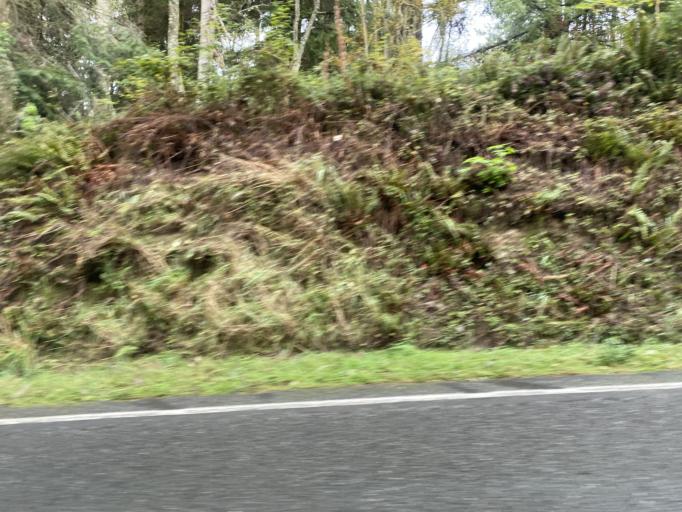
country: US
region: Washington
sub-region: Island County
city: Freeland
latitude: 48.0660
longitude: -122.5036
